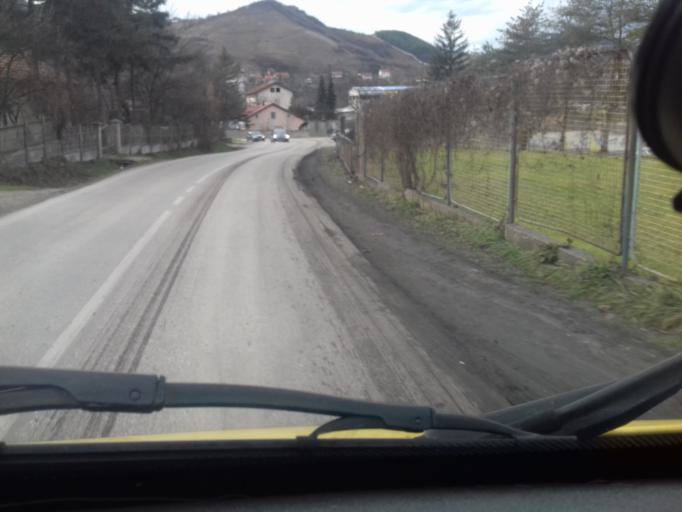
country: BA
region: Federation of Bosnia and Herzegovina
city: Zenica
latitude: 44.1886
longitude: 17.9272
